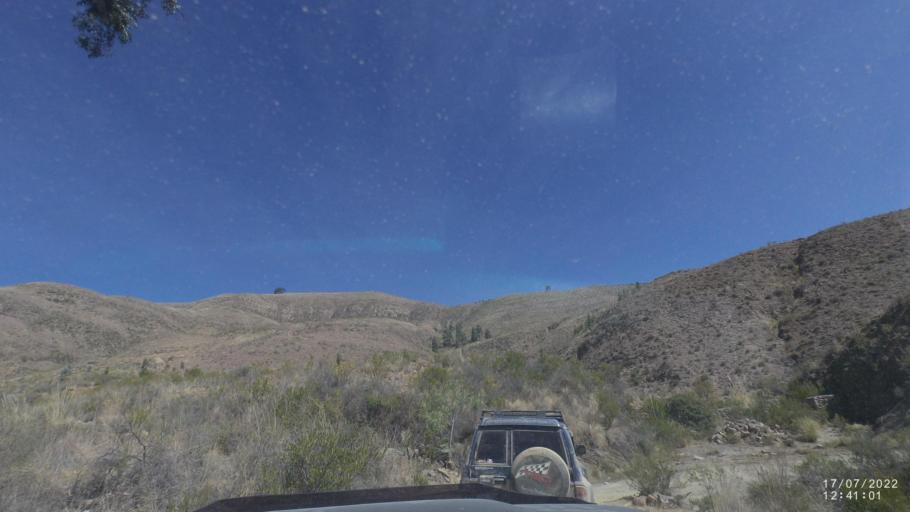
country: BO
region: Cochabamba
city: Tarata
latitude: -17.6602
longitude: -66.1305
